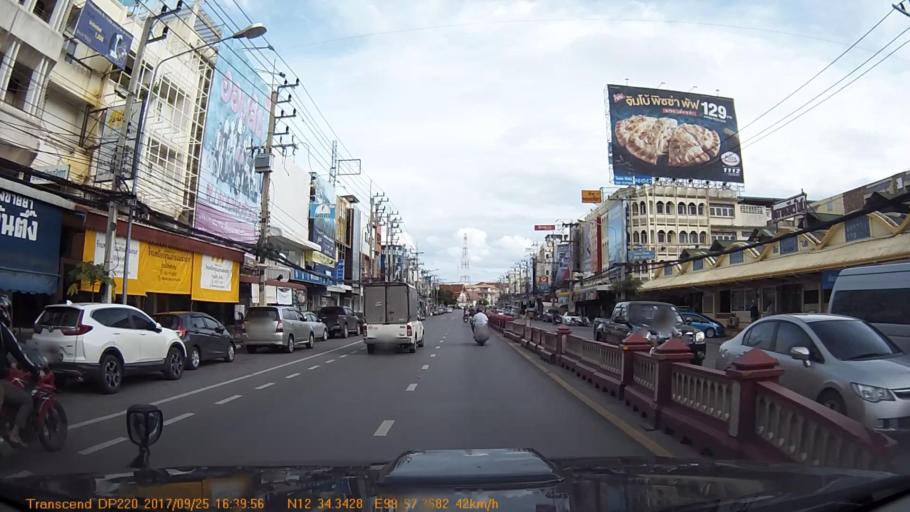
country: TH
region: Prachuap Khiri Khan
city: Hua Hin
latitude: 12.5722
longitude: 99.9563
